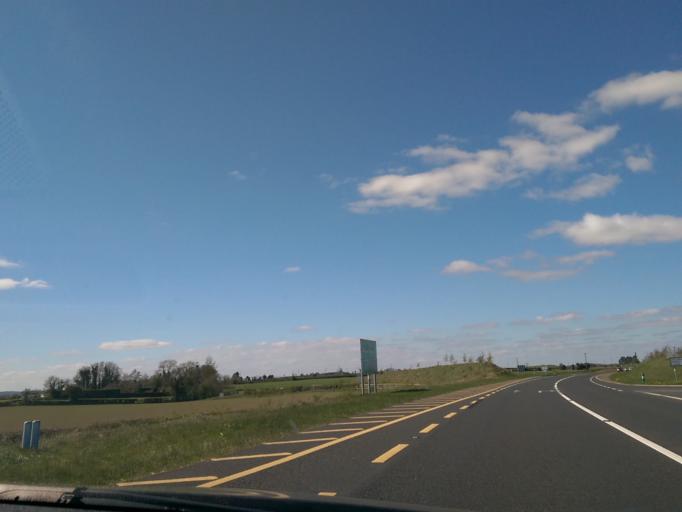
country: IE
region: Leinster
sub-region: Kildare
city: Athy
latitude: 52.9882
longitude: -6.9438
